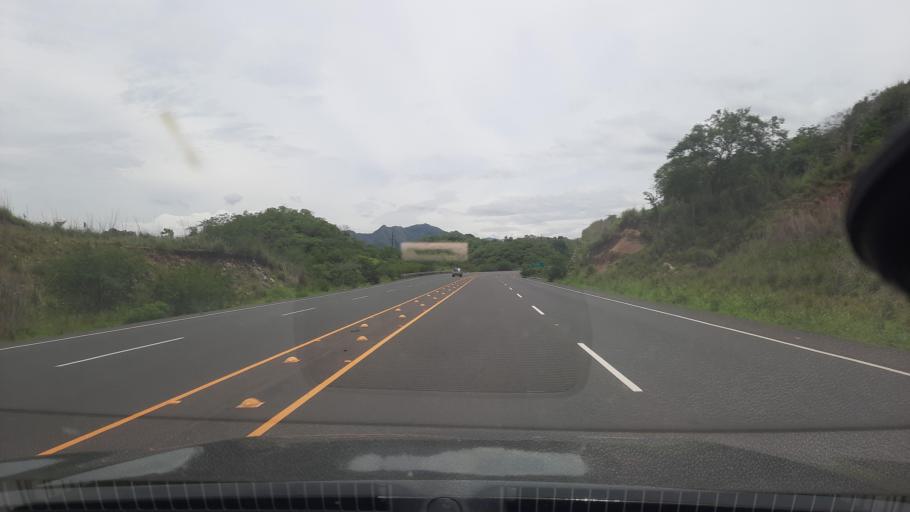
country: HN
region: Valle
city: Aramecina
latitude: 13.8012
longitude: -87.7056
